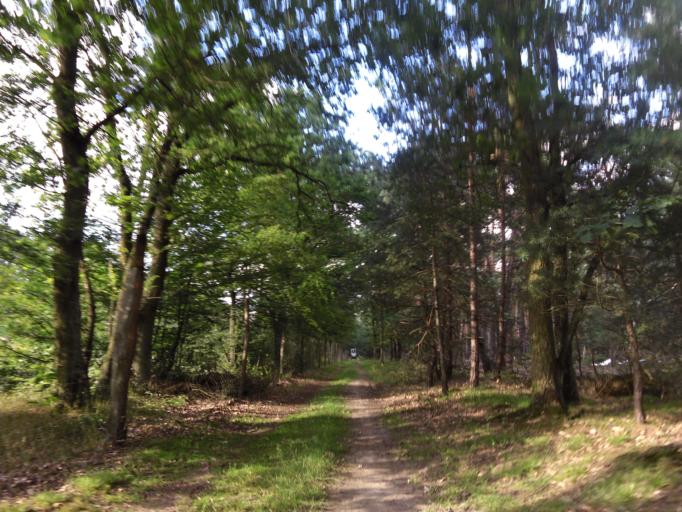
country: DE
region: Hesse
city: Niederrad
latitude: 50.0499
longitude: 8.6148
